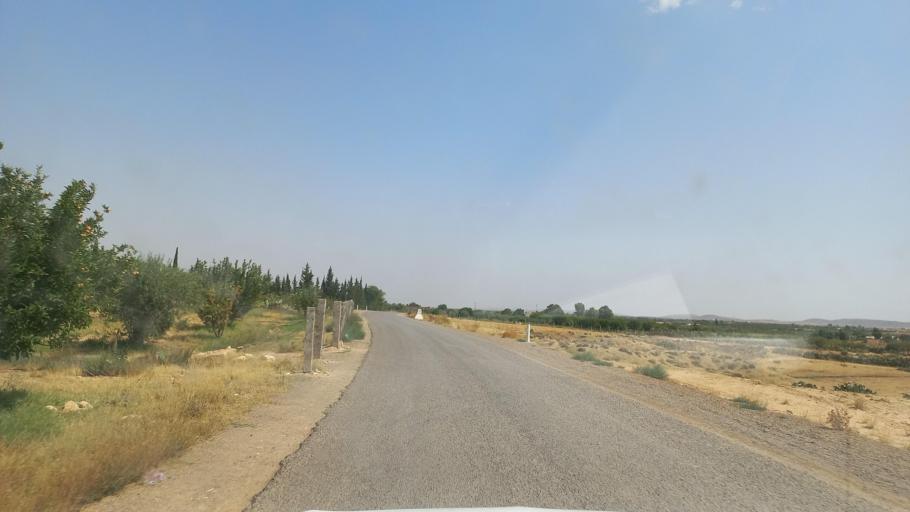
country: TN
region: Al Qasrayn
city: Kasserine
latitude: 35.2406
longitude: 9.0299
